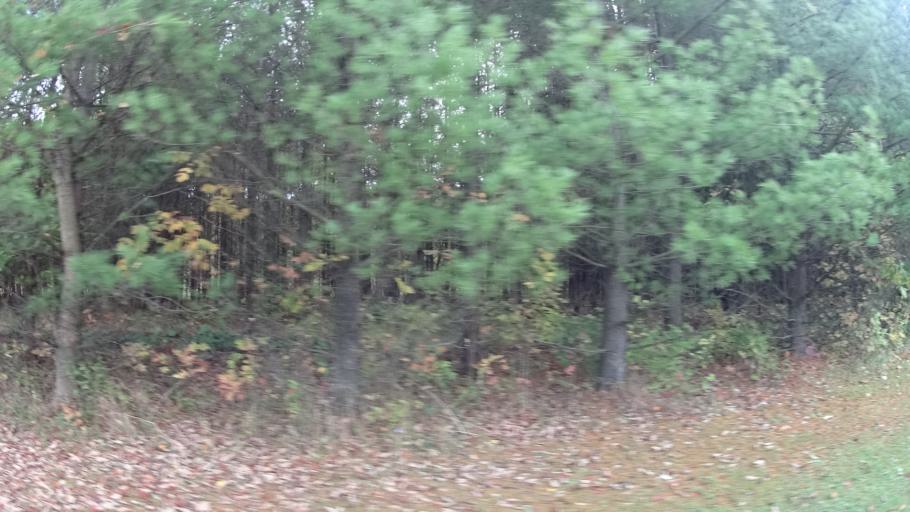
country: US
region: Ohio
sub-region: Lorain County
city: Grafton
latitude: 41.3032
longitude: -82.0813
